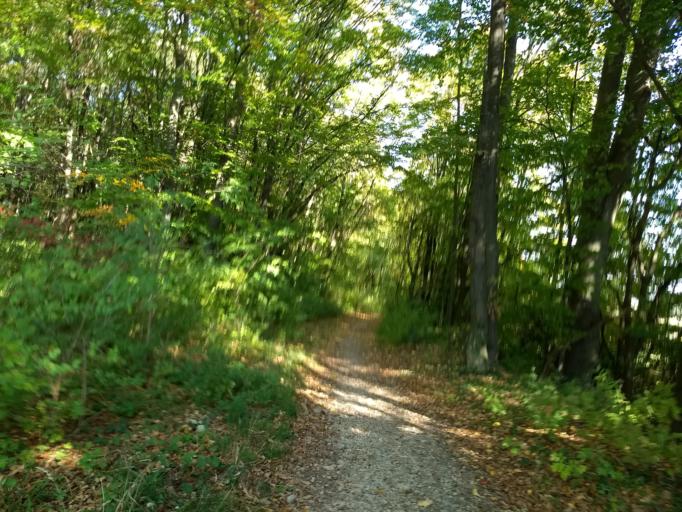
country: AT
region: Lower Austria
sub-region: Politischer Bezirk Modling
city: Giesshubl
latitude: 48.1058
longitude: 16.2398
